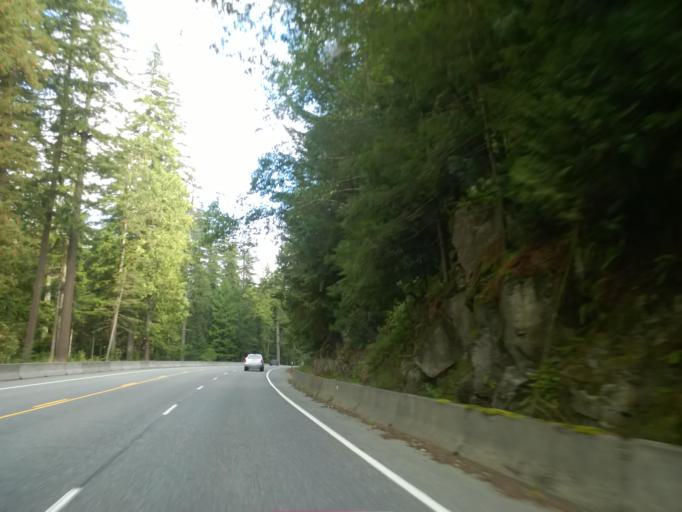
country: US
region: Washington
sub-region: Snohomish County
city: Gold Bar
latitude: 47.7170
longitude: -121.2147
